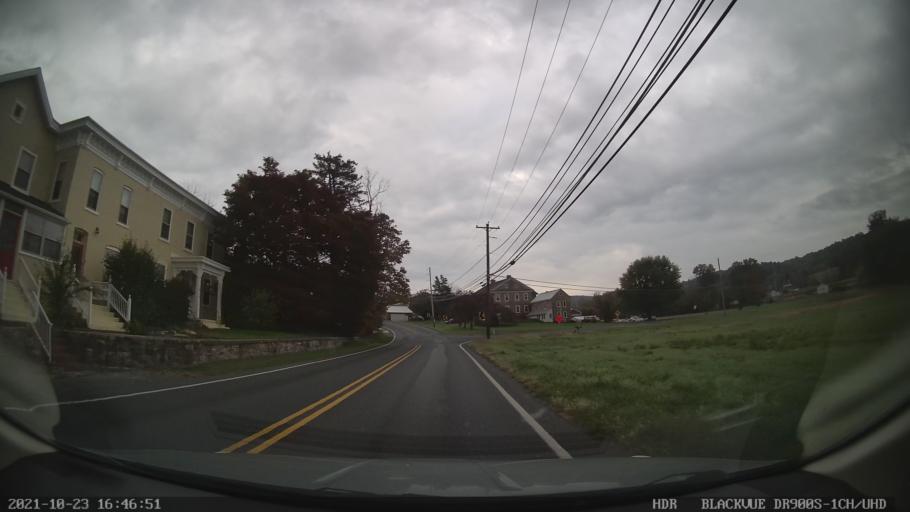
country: US
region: Pennsylvania
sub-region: Berks County
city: Red Lion
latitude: 40.4913
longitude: -75.6453
